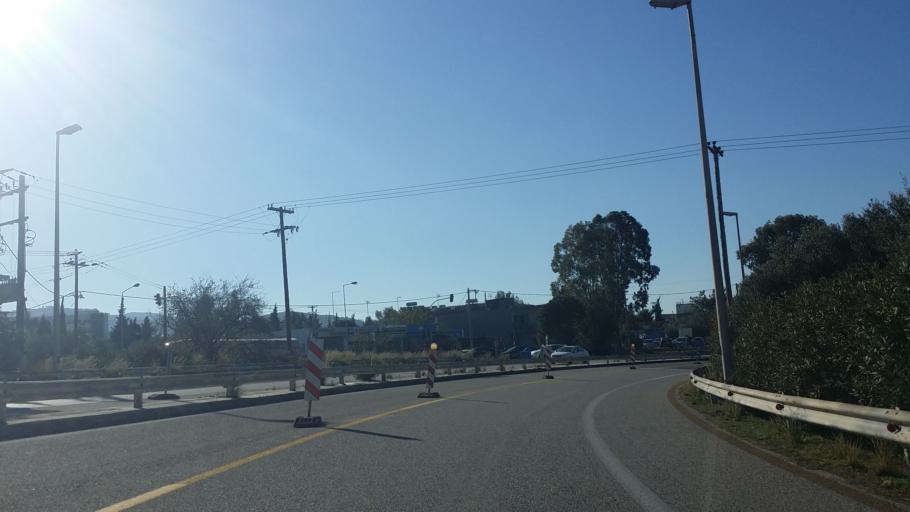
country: GR
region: West Greece
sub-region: Nomos Achaias
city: Rio
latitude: 38.2970
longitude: 21.7932
